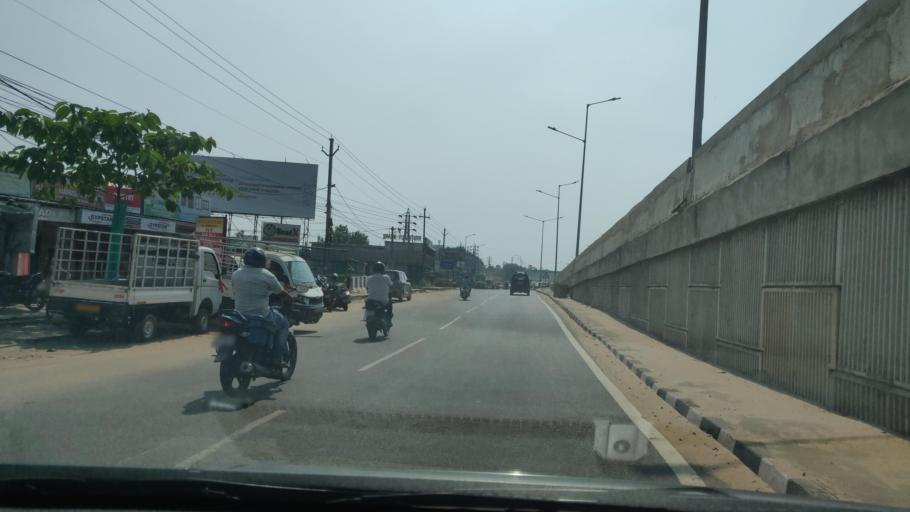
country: IN
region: Odisha
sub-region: Khordha
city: Bhubaneshwar
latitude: 20.2521
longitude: 85.7852
